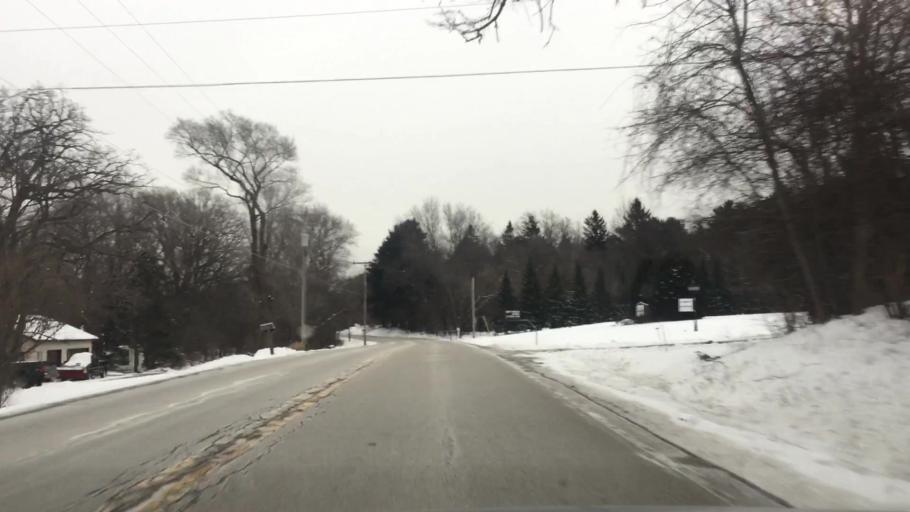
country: US
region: Wisconsin
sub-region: Waukesha County
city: Hartland
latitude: 43.0494
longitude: -88.3213
